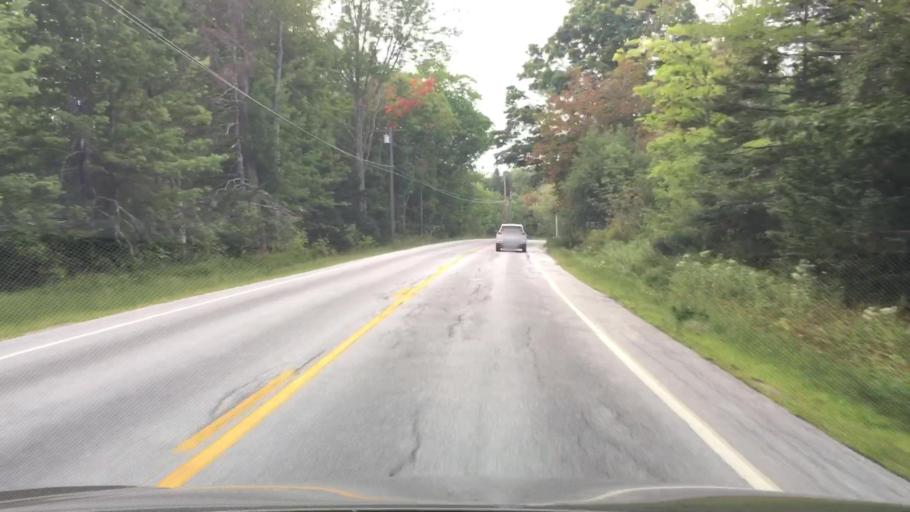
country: US
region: Maine
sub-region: Hancock County
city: Penobscot
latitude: 44.4311
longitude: -68.6054
